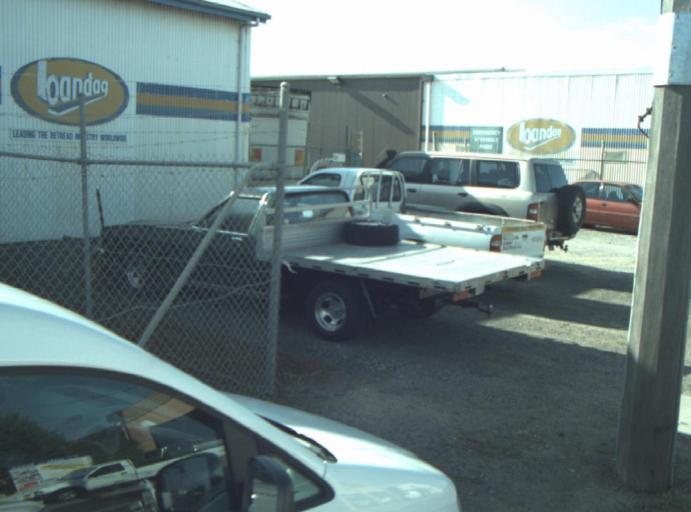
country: AU
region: Victoria
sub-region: Greater Geelong
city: Bell Park
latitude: -38.1157
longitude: 144.3490
